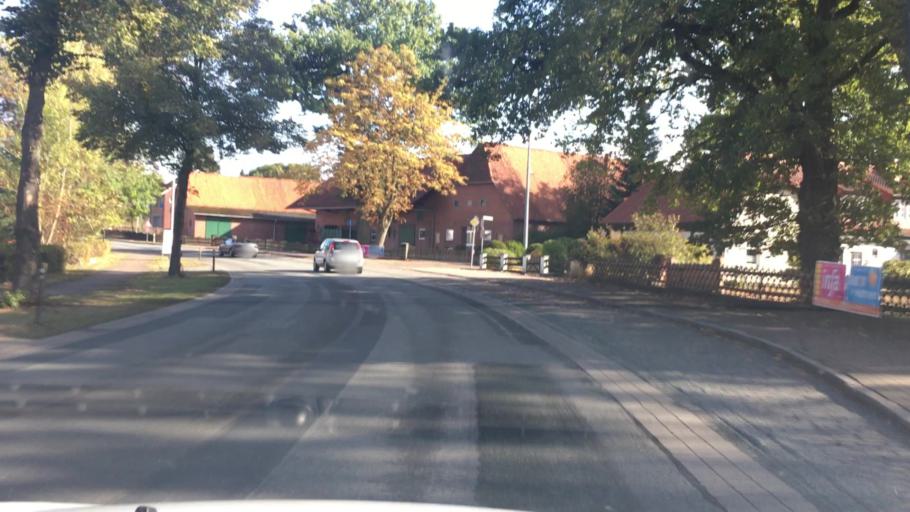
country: DE
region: Lower Saxony
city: Borstel
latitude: 52.6686
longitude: 8.9734
